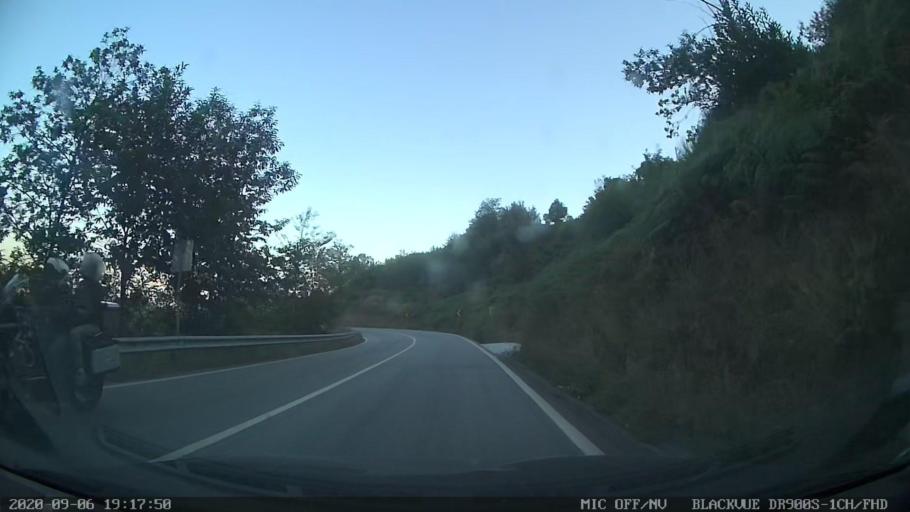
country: PT
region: Porto
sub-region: Baiao
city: Valadares
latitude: 41.1929
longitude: -7.9466
